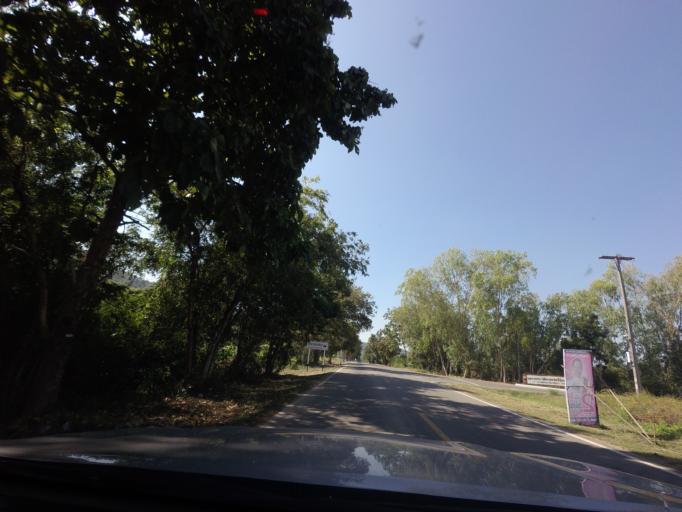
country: TH
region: Sukhothai
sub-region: Amphoe Si Satchanalai
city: Si Satchanalai
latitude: 17.4195
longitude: 99.7877
